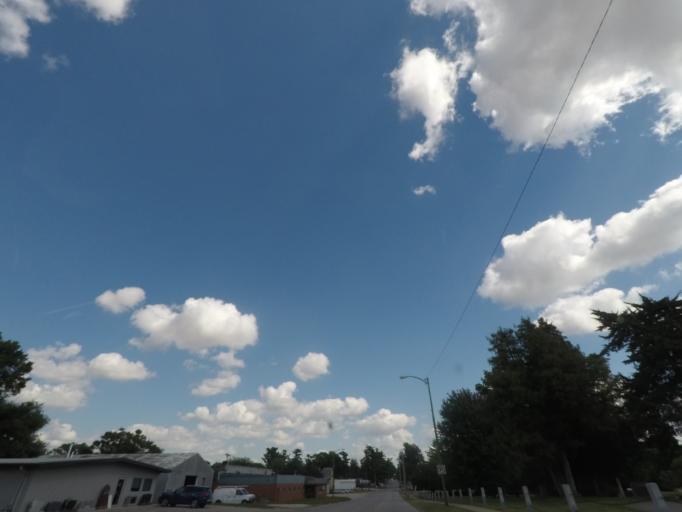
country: US
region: Iowa
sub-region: Story County
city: Nevada
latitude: 42.0227
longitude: -93.4620
